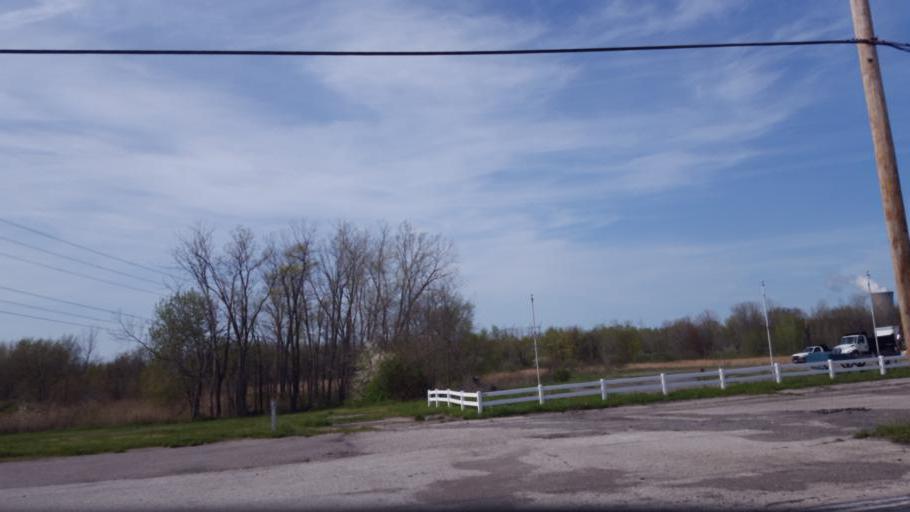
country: US
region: Ohio
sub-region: Lake County
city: Perry
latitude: 41.7778
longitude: -81.1542
